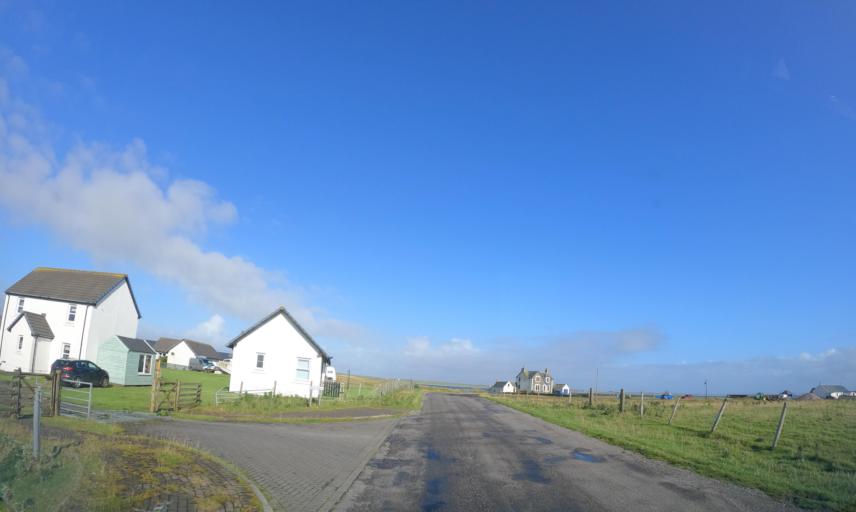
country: GB
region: Scotland
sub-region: Eilean Siar
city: Barra
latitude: 56.5065
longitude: -6.8018
